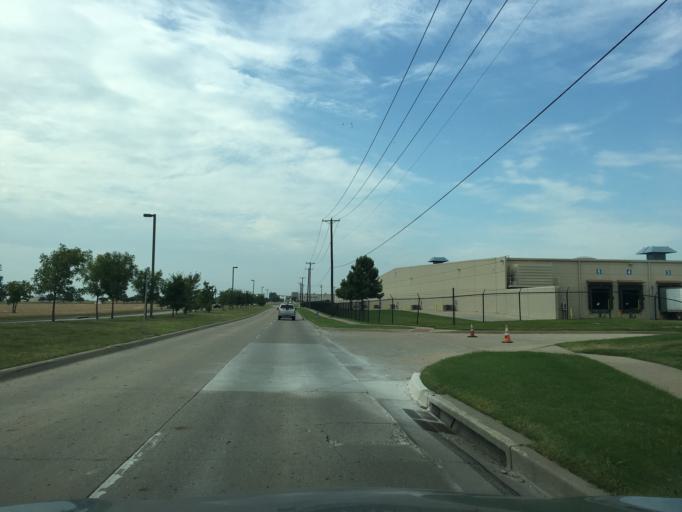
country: US
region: Texas
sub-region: Collin County
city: McKinney
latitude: 33.1815
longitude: -96.5984
